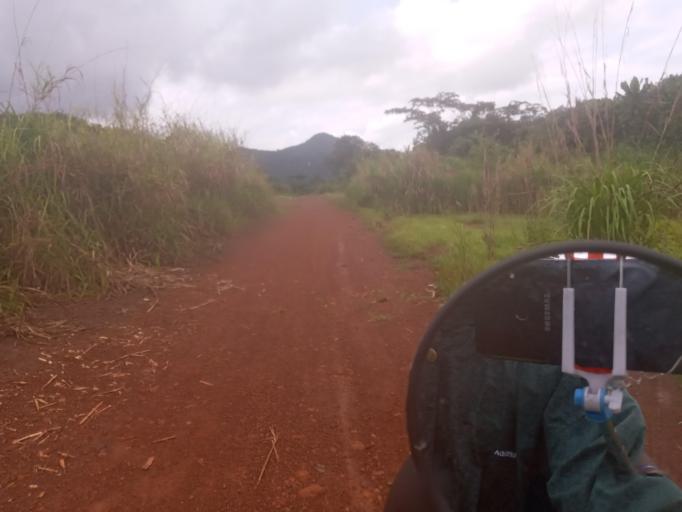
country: SL
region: Northern Province
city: Bumbuna
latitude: 8.9230
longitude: -11.7429
